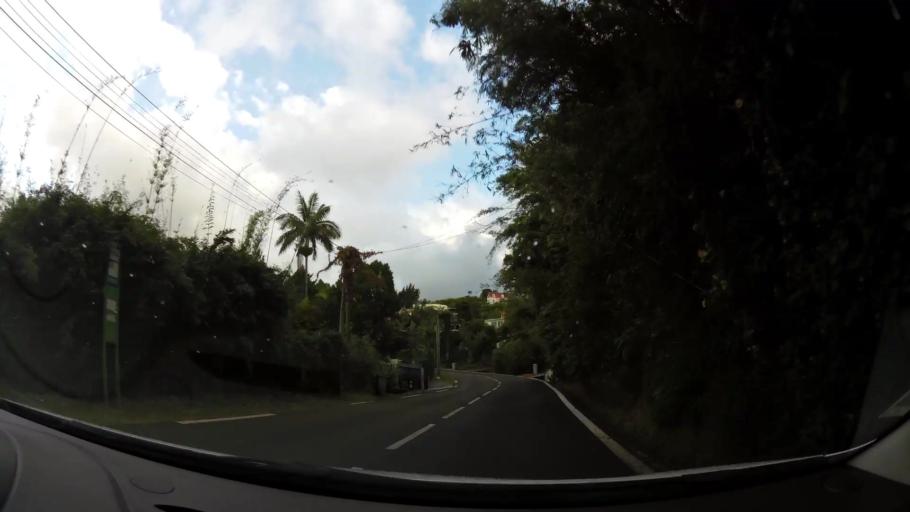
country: RE
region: Reunion
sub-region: Reunion
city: Saint-Denis
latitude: -20.9117
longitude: 55.4403
